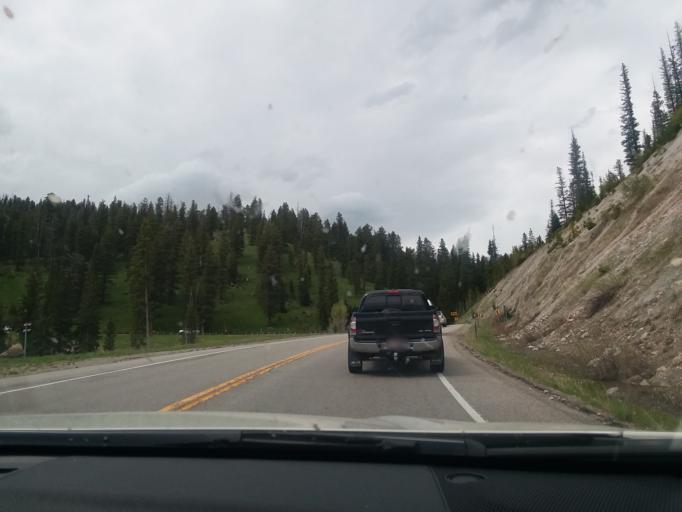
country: US
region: Wyoming
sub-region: Teton County
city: Wilson
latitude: 43.5038
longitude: -110.9224
